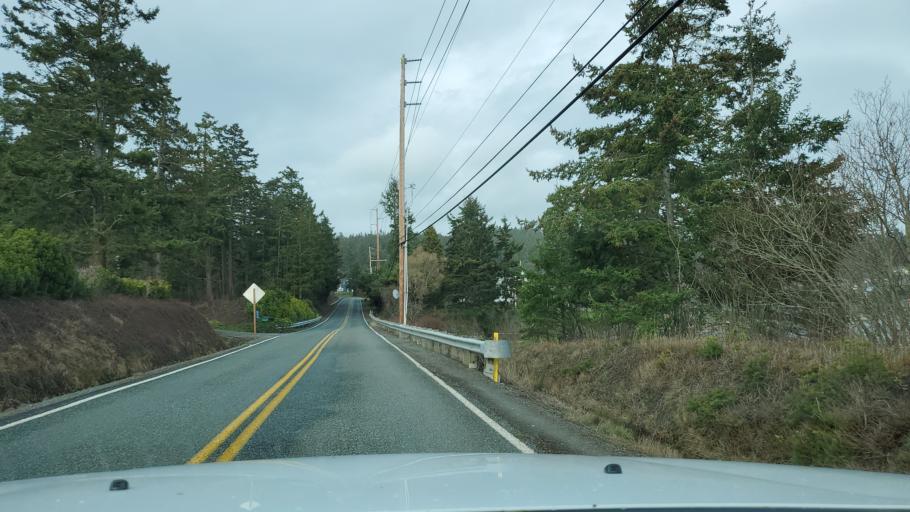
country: US
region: Washington
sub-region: Skagit County
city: Anacortes
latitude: 48.4231
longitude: -122.6102
